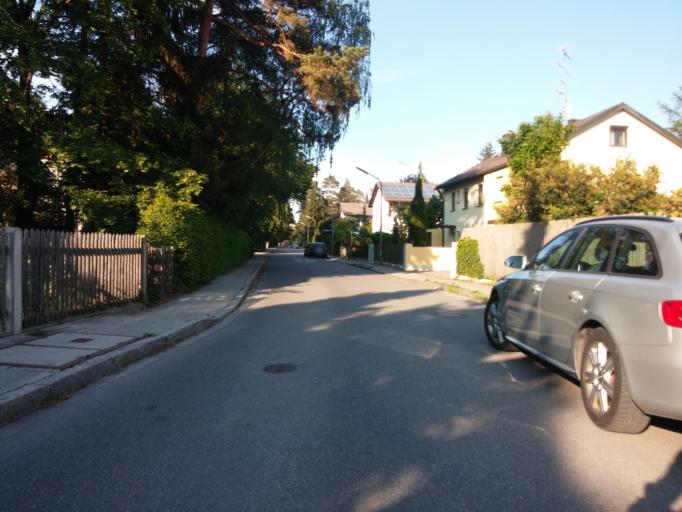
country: DE
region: Bavaria
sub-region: Upper Bavaria
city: Vaterstetten
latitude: 48.1022
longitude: 11.7814
